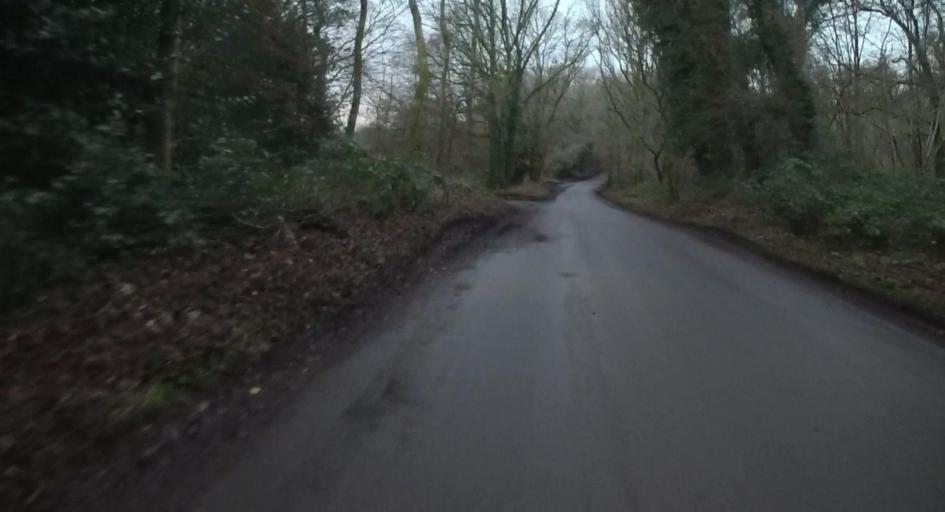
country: GB
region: England
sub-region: Hampshire
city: Four Marks
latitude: 51.0584
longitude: -1.1009
